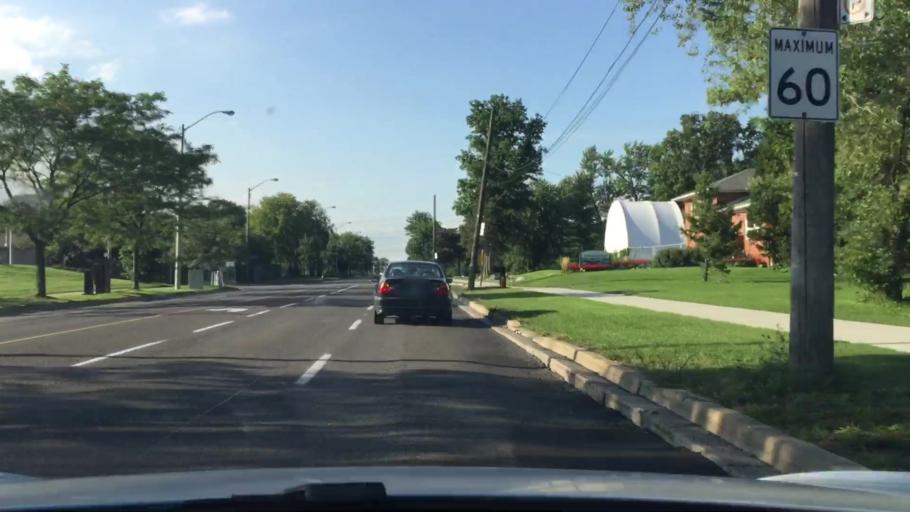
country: CA
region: Ontario
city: Scarborough
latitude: 43.8036
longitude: -79.3088
